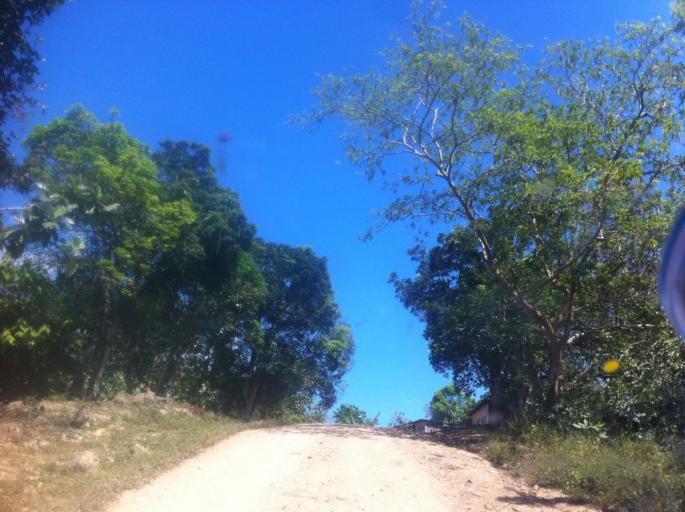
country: CR
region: Alajuela
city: Los Chiles
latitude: 11.2512
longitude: -84.4406
